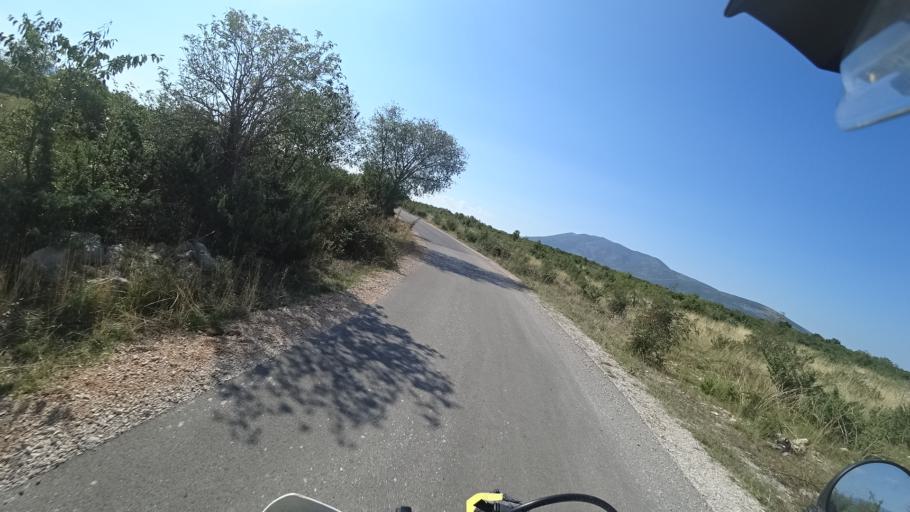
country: HR
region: Sibensko-Kniniska
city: Knin
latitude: 44.0046
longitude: 16.1934
